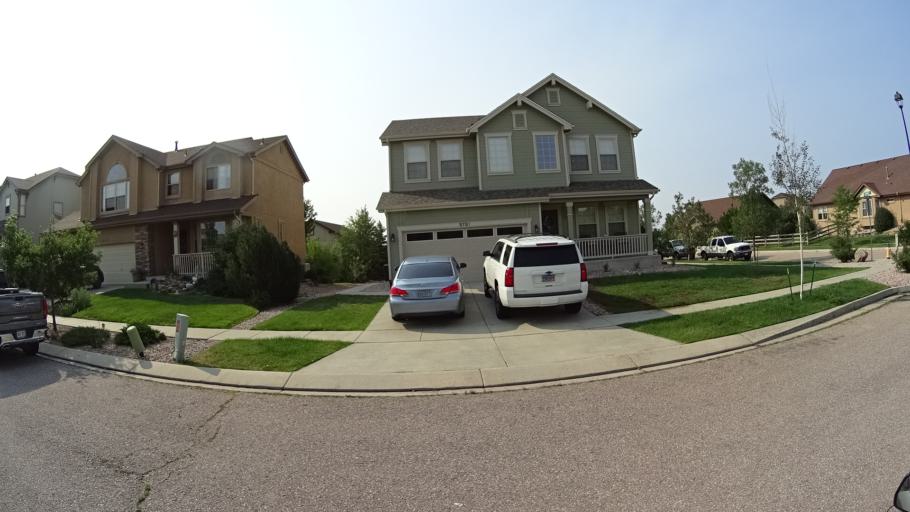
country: US
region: Colorado
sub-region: El Paso County
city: Black Forest
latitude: 38.9600
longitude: -104.7203
